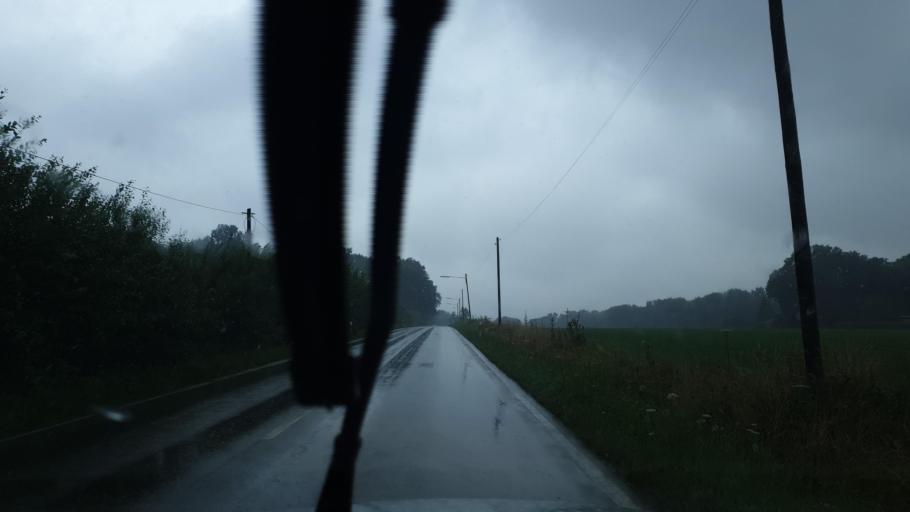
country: DE
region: North Rhine-Westphalia
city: Loehne
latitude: 52.1747
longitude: 8.6858
